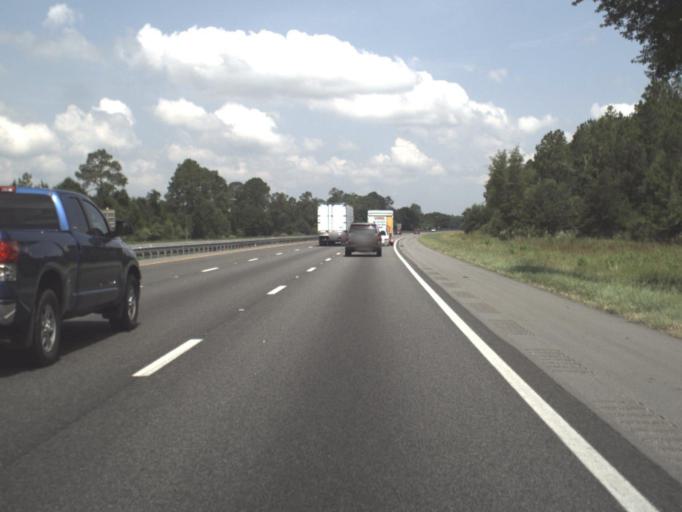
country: US
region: Georgia
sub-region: Echols County
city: Statenville
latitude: 30.6223
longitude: -83.1654
